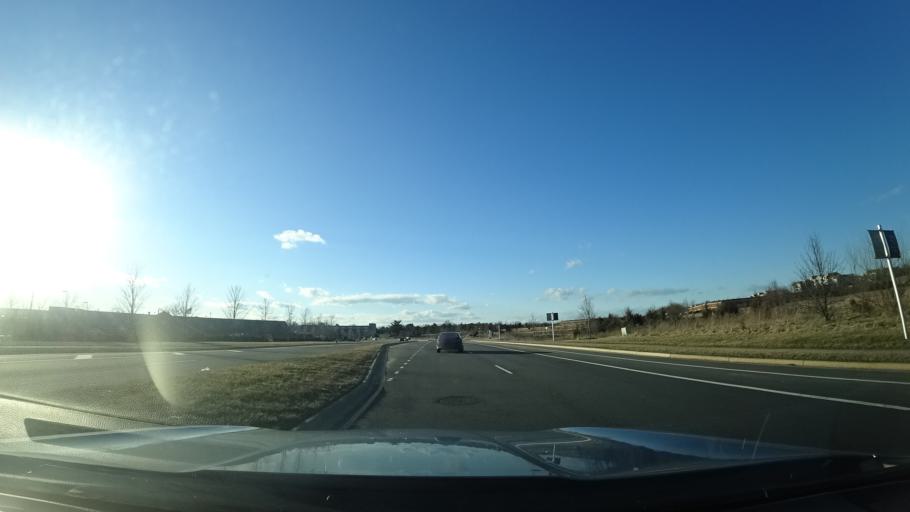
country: US
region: Virginia
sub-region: Loudoun County
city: University Center
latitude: 39.0599
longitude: -77.4476
